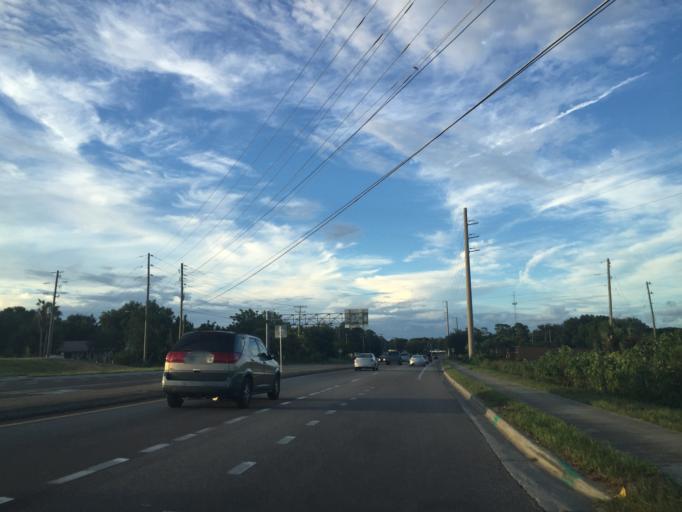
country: US
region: Florida
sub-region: Lake County
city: Tavares
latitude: 28.7852
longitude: -81.7483
